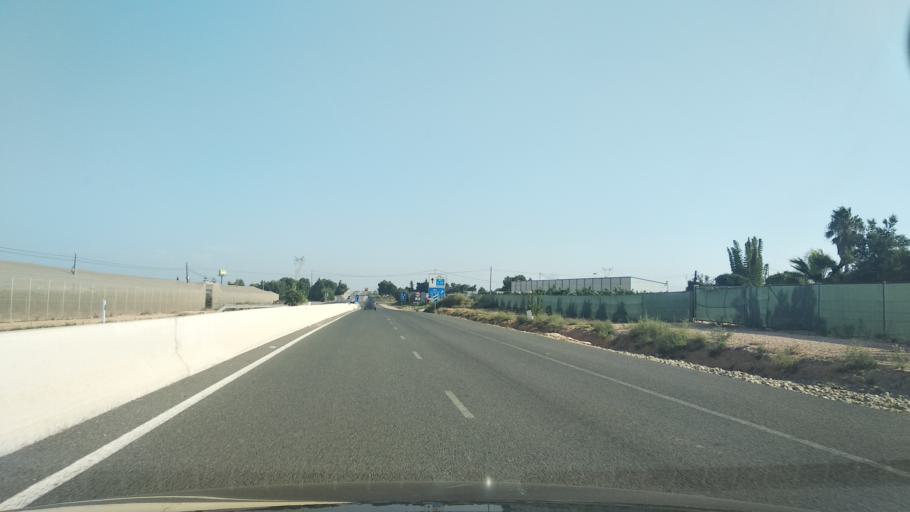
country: ES
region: Murcia
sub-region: Murcia
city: San Javier
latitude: 37.8192
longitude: -0.8469
